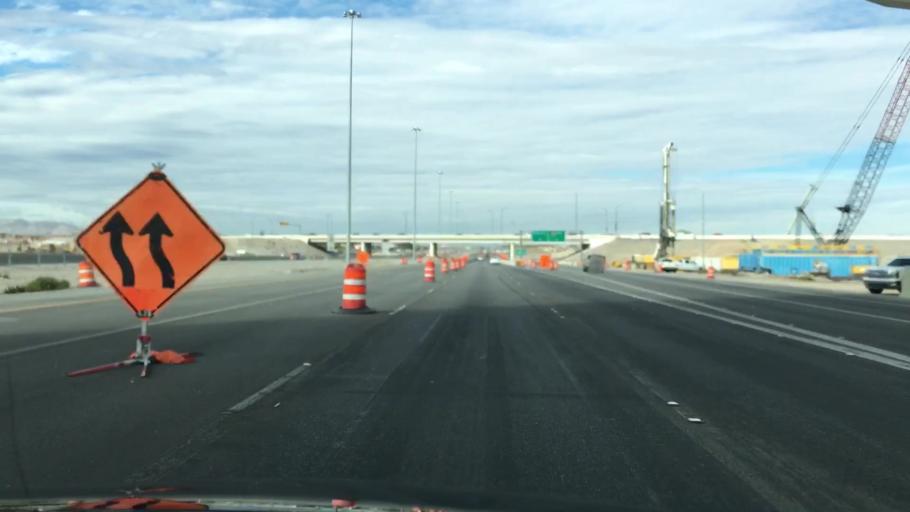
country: US
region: Nevada
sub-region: Clark County
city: Las Vegas
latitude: 36.2755
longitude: -115.2648
